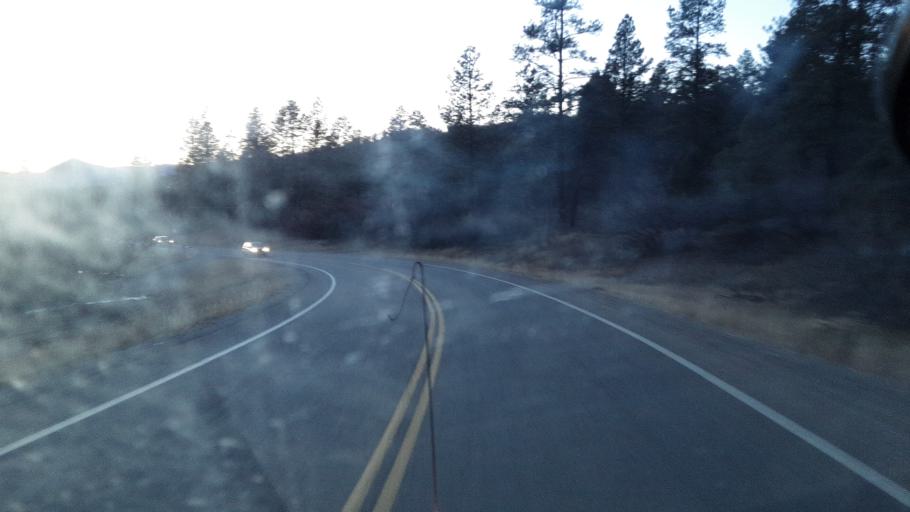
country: US
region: Colorado
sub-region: La Plata County
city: Durango
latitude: 37.3131
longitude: -107.8012
